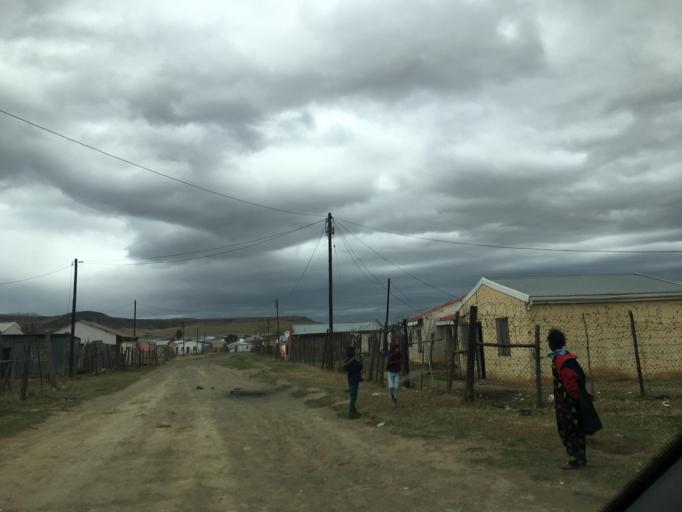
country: ZA
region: Eastern Cape
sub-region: Chris Hani District Municipality
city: Cala
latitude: -31.5334
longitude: 27.6998
